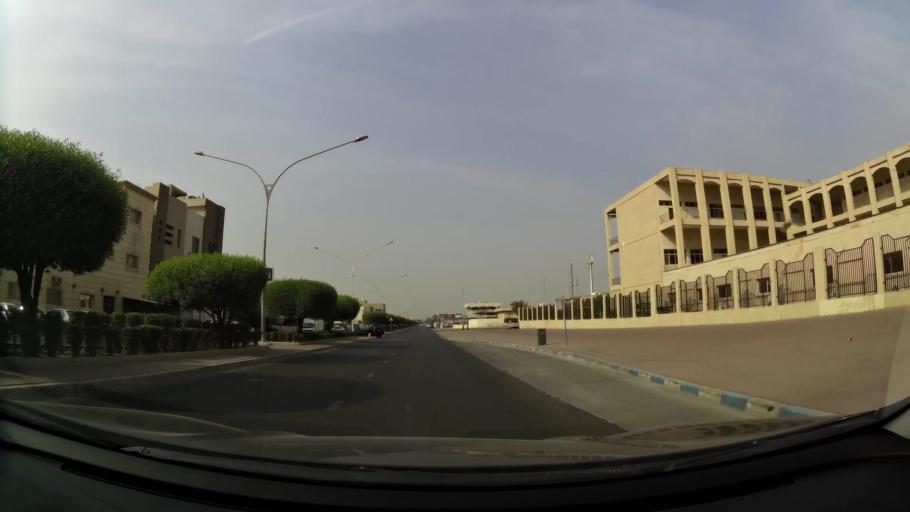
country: KW
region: Al Farwaniyah
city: Al Farwaniyah
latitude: 29.2922
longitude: 47.9544
